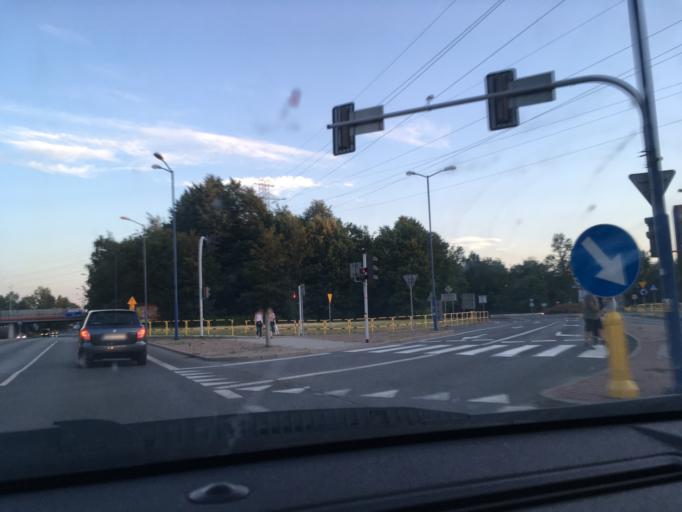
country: PL
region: Silesian Voivodeship
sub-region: Katowice
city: Katowice
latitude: 50.2481
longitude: 19.0259
